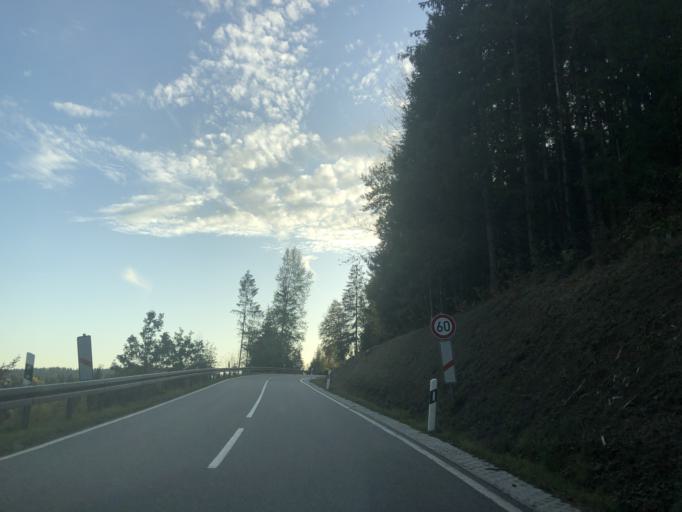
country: DE
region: Bavaria
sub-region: Lower Bavaria
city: Zwiesel
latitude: 49.0111
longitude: 13.2041
